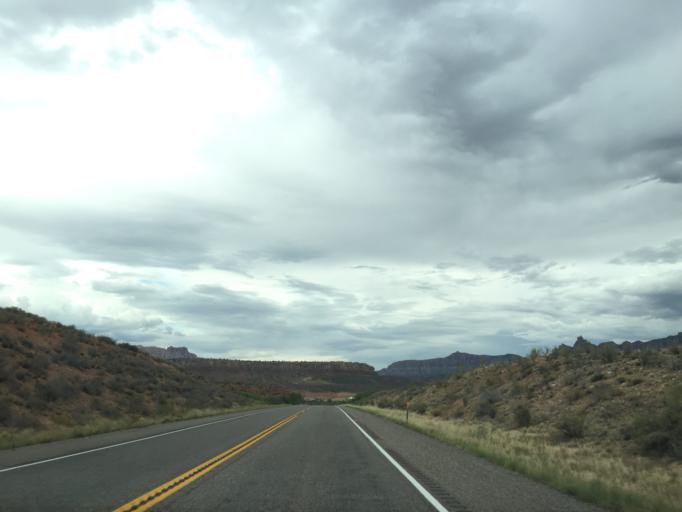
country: US
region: Utah
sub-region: Washington County
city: LaVerkin
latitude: 37.1713
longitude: -113.0863
